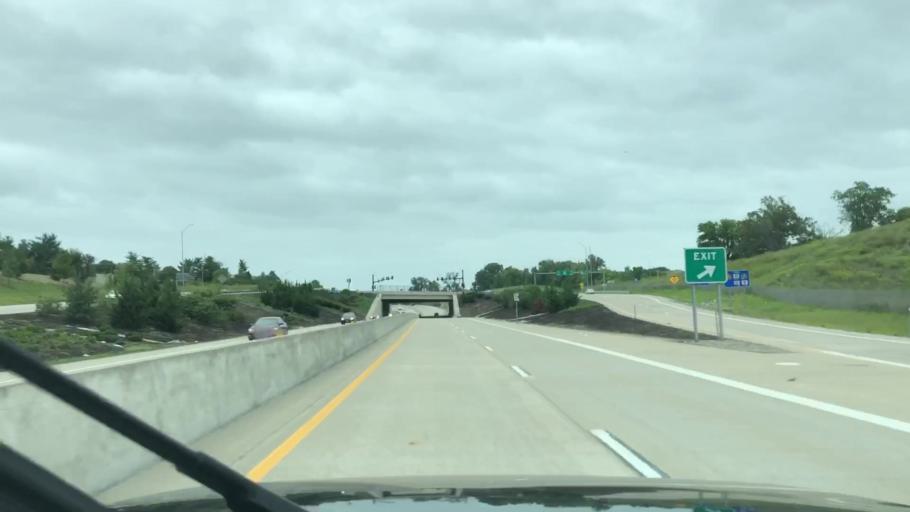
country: US
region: Missouri
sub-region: Saint Louis County
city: Maryland Heights
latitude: 38.6785
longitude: -90.4933
